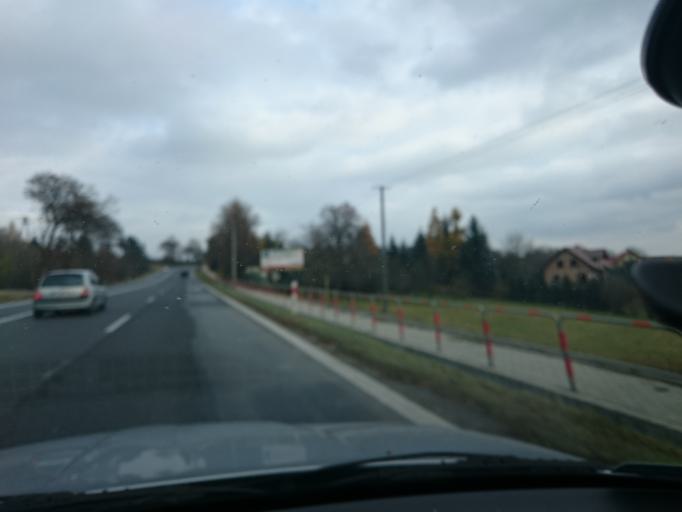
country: PL
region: Lesser Poland Voivodeship
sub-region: Powiat krakowski
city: Michalowice
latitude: 50.1778
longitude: 19.9895
